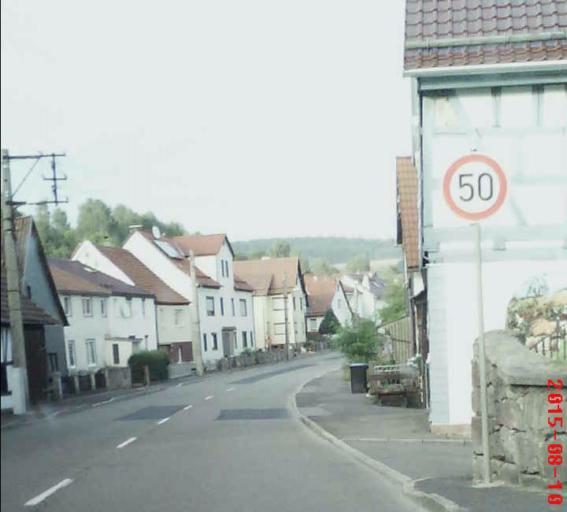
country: DE
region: Thuringia
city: Schmeheim
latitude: 50.6006
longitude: 10.5732
